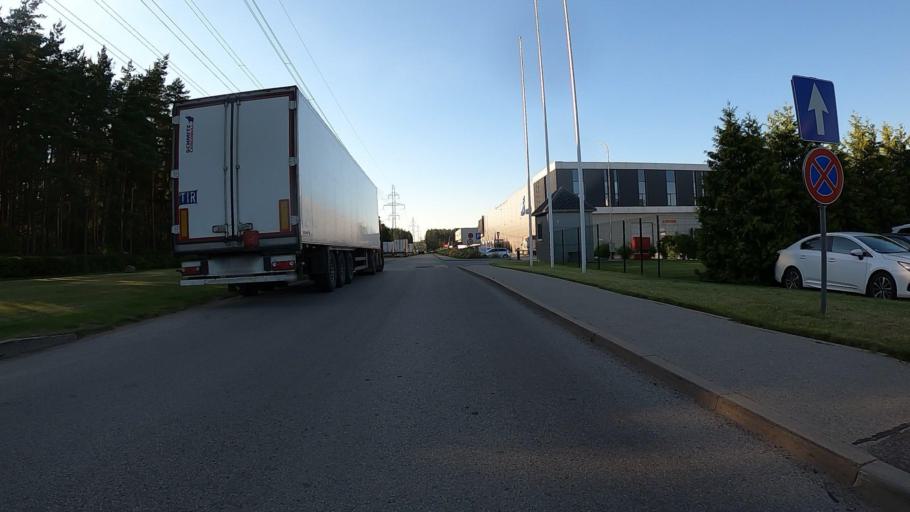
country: LV
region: Stopini
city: Ulbroka
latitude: 56.9340
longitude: 24.2359
